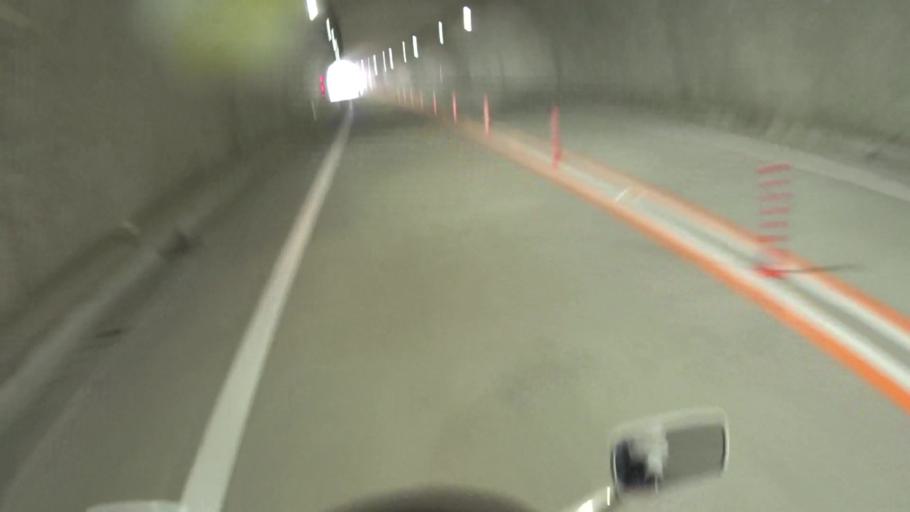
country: JP
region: Kyoto
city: Ayabe
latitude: 35.2575
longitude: 135.3426
